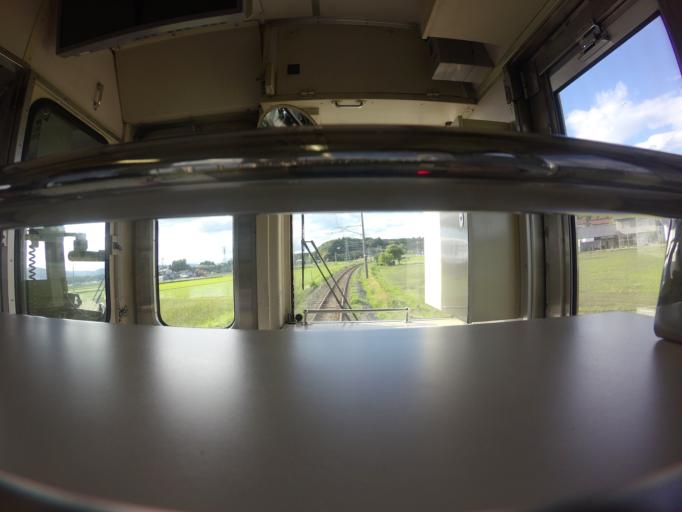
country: JP
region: Fukushima
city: Namie
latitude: 37.6087
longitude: 140.9871
